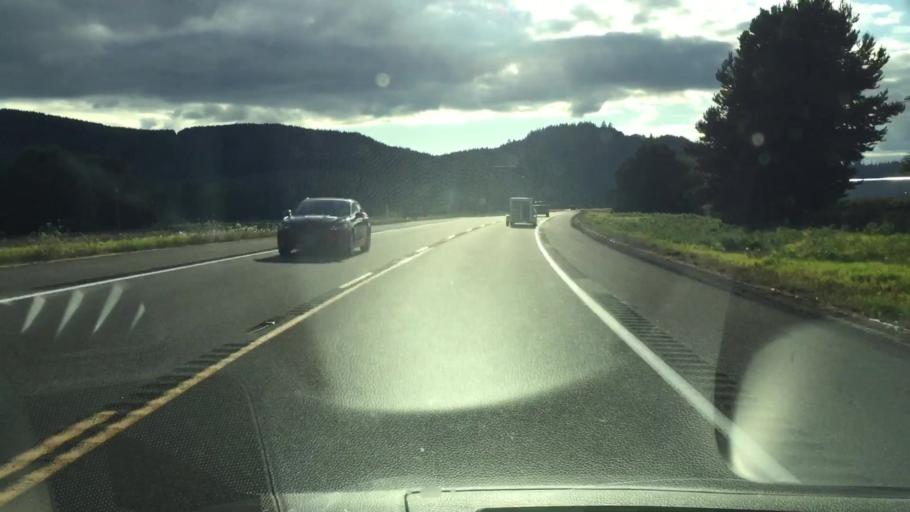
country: US
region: Washington
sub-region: Lewis County
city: Morton
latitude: 46.5324
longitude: -122.5248
